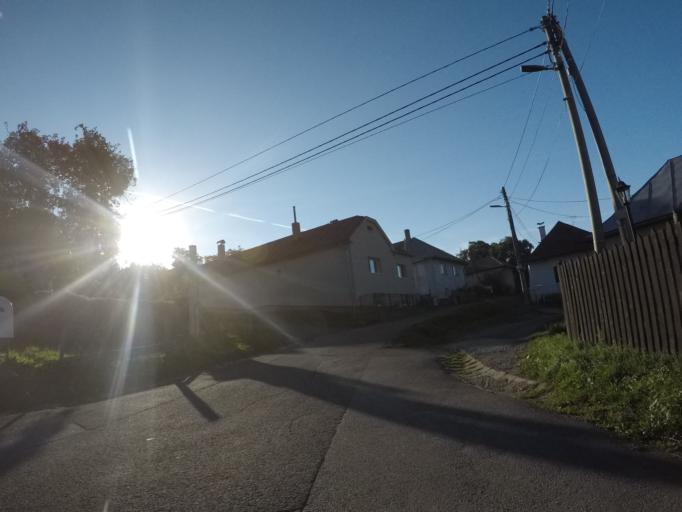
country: SK
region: Kosicky
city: Kosice
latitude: 48.7441
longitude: 21.1265
